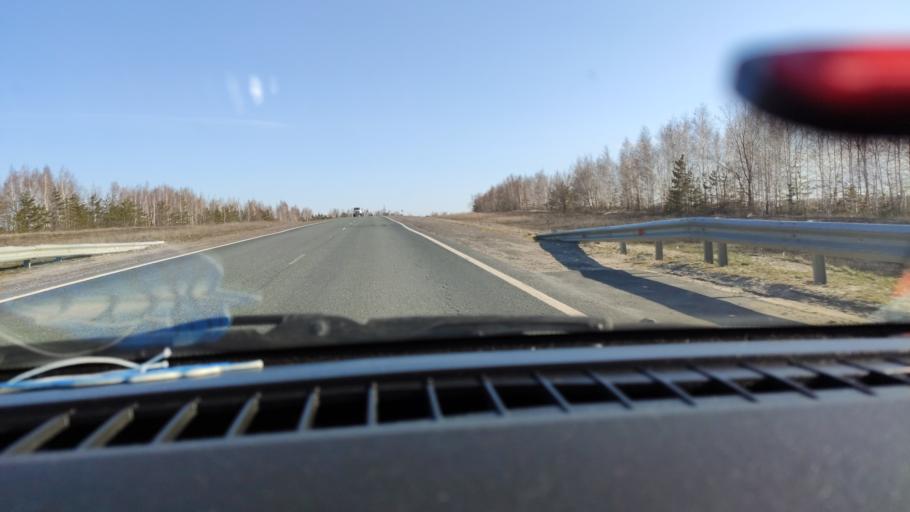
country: RU
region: Saratov
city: Dukhovnitskoye
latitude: 52.8334
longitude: 48.2404
